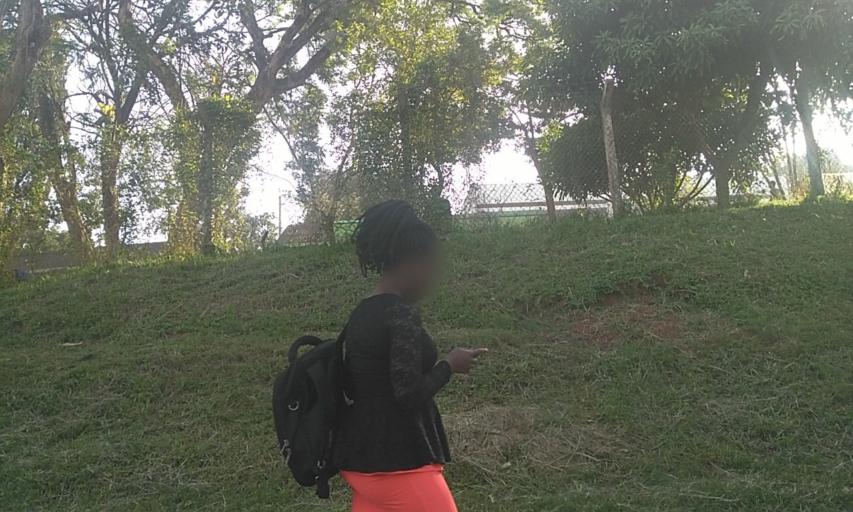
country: UG
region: Central Region
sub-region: Kampala District
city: Kampala
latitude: 0.3384
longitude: 32.5987
